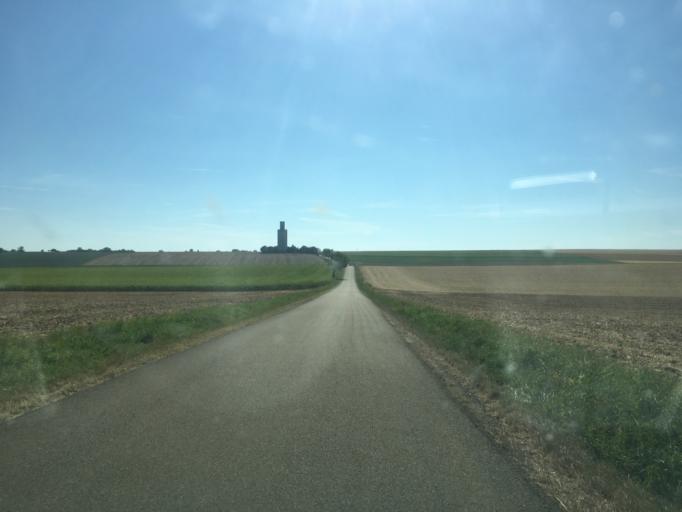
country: FR
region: Bourgogne
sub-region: Departement de l'Yonne
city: Fleury-la-Vallee
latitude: 47.9166
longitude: 3.4162
